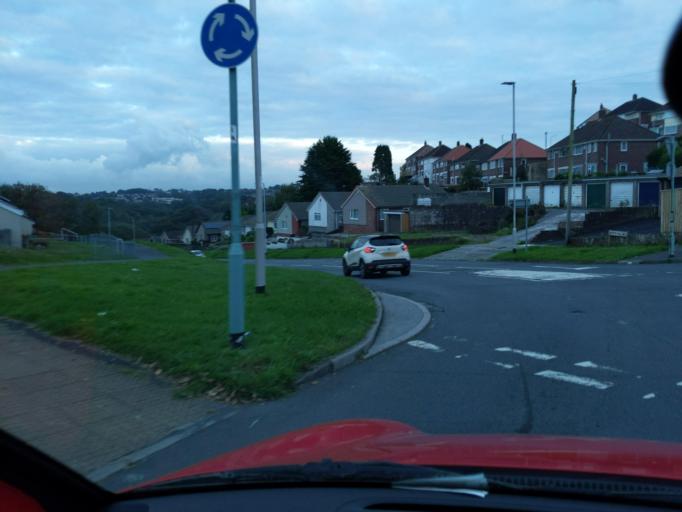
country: GB
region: England
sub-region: Cornwall
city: Torpoint
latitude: 50.4029
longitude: -4.1771
